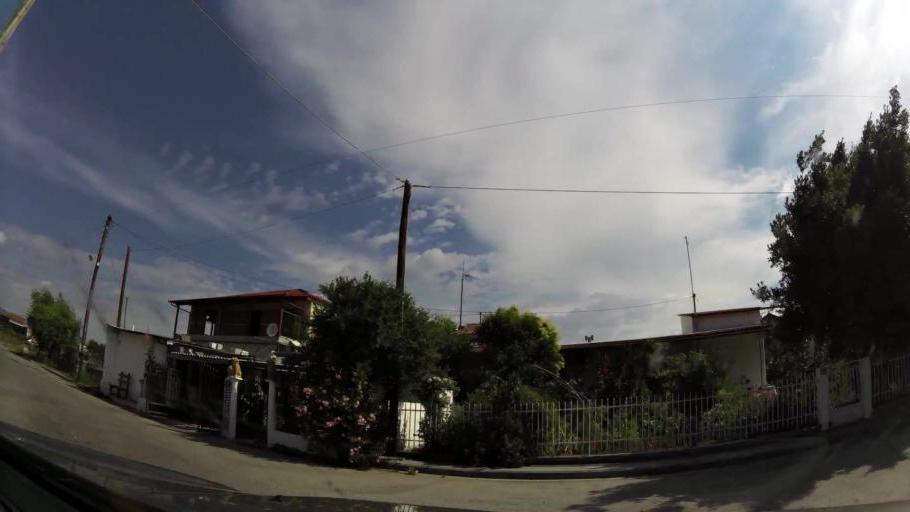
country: GR
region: Central Macedonia
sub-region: Nomos Pierias
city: Katerini
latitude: 40.2827
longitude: 22.4968
